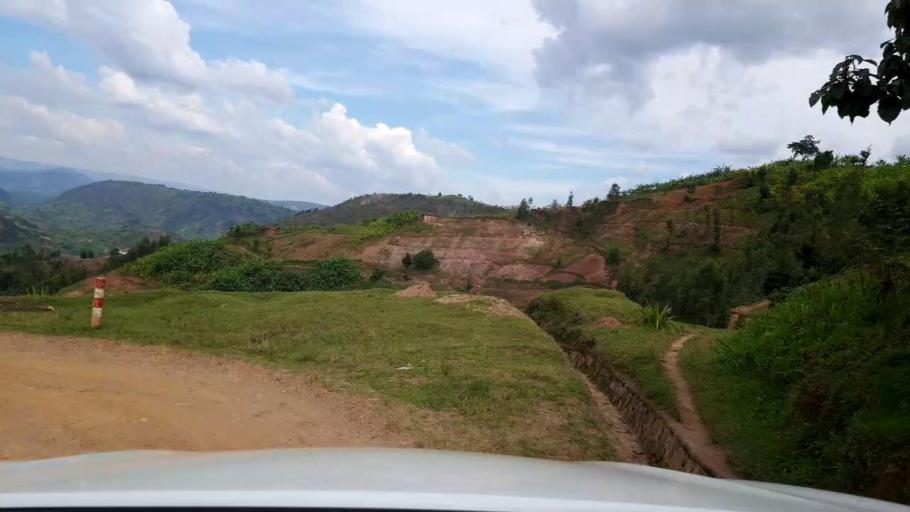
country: RW
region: Southern Province
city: Gitarama
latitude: -1.9821
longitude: 29.7113
